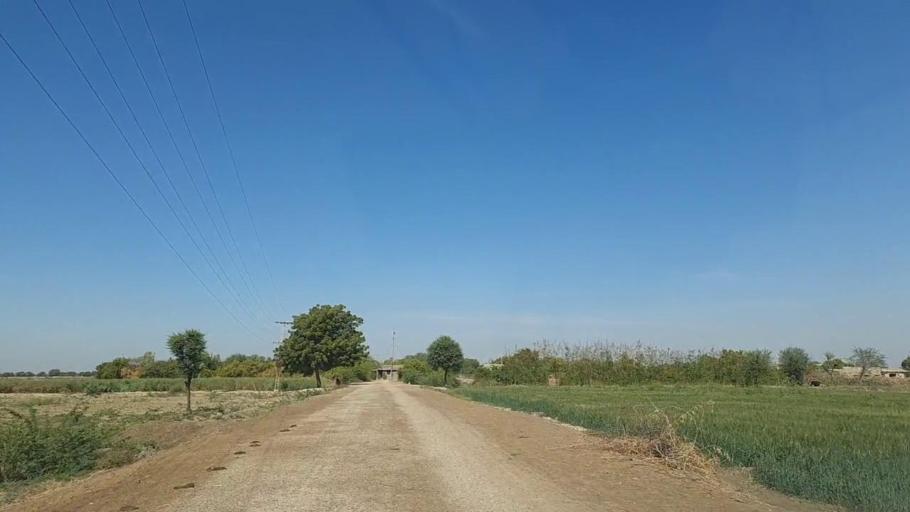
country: PK
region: Sindh
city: Samaro
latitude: 25.3062
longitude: 69.5019
